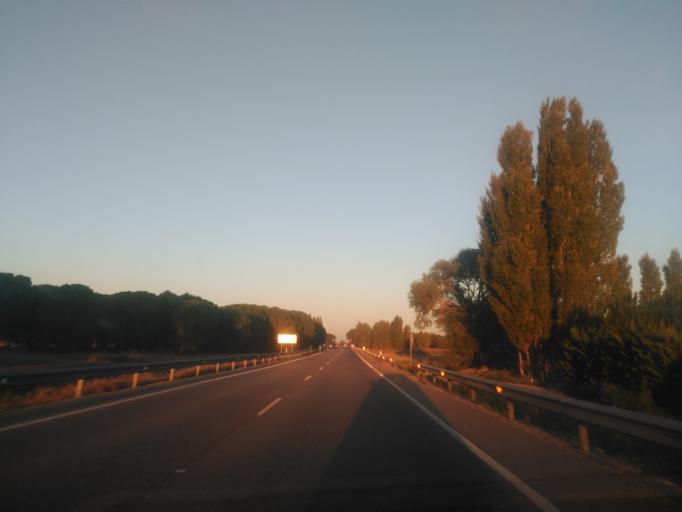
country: ES
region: Castille and Leon
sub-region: Provincia de Valladolid
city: Sardon de Duero
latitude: 41.6053
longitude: -4.4498
